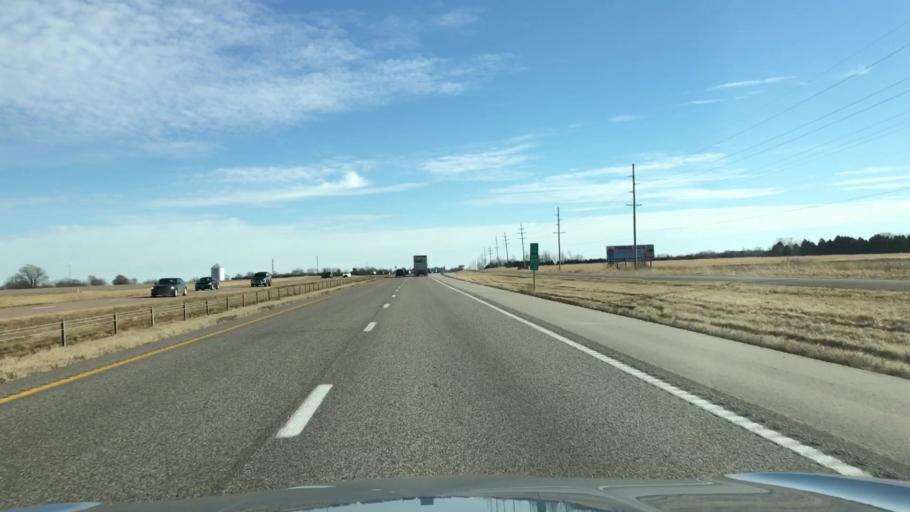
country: US
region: Missouri
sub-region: Montgomery County
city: Montgomery City
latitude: 38.8854
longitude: -91.4064
